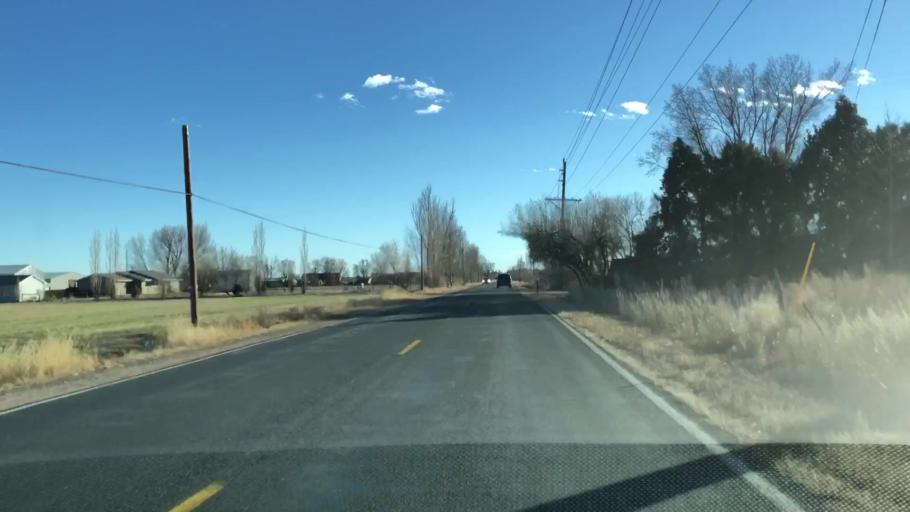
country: US
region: Colorado
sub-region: Larimer County
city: Fort Collins
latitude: 40.5497
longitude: -104.9824
